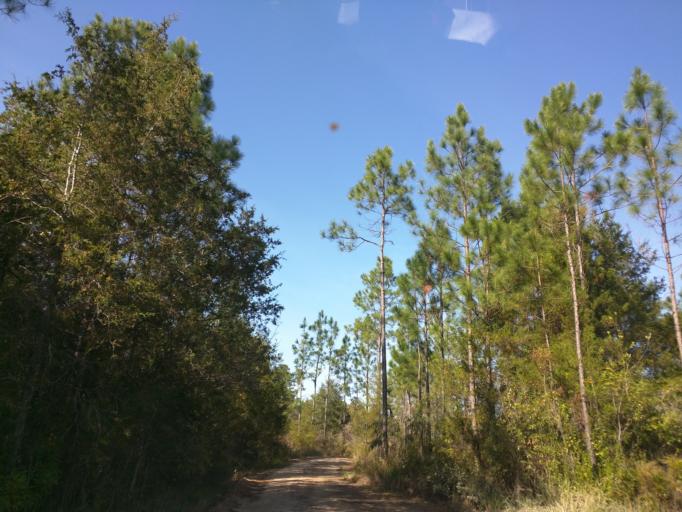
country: US
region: Florida
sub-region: Escambia County
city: Cantonment
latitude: 30.5453
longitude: -87.4309
